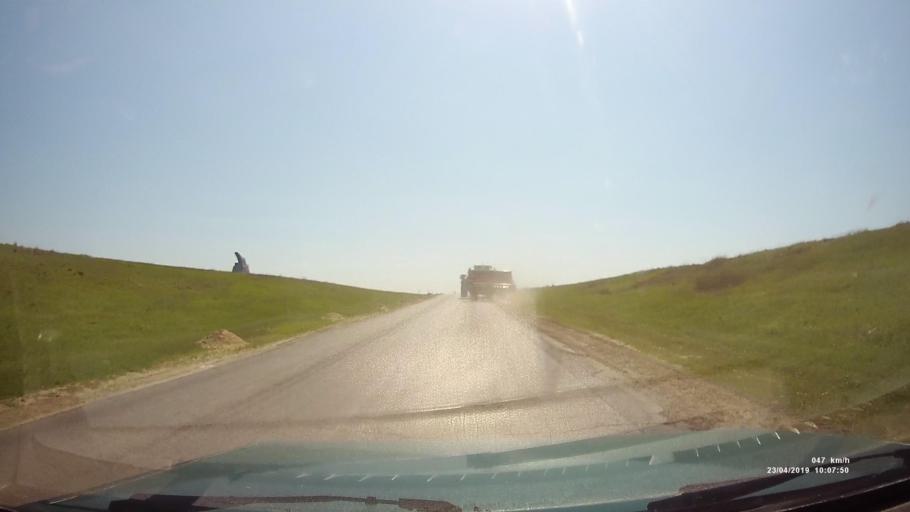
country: RU
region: Rostov
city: Sovetskoye
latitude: 46.7225
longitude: 42.2591
